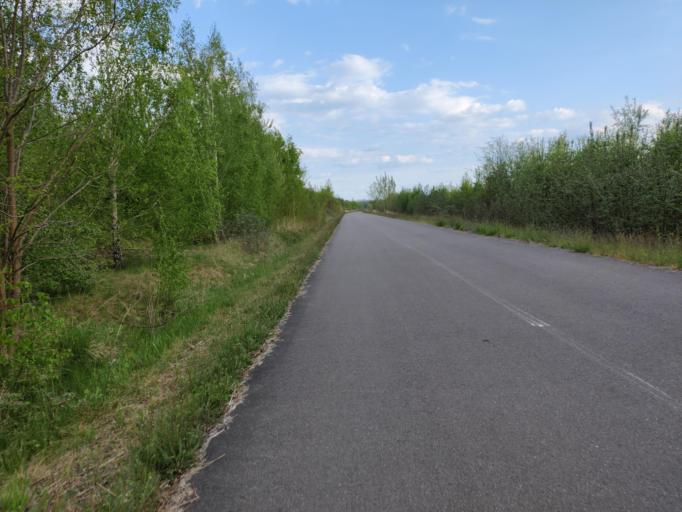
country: DE
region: Saxony
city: Rotha
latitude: 51.2202
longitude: 12.4430
